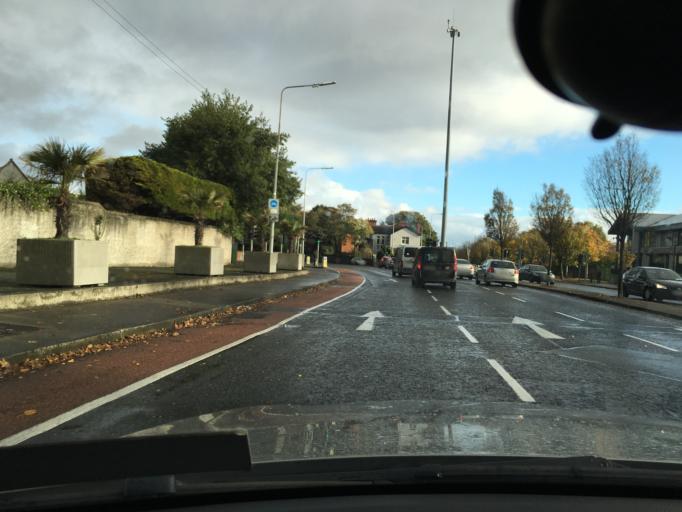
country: IE
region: Leinster
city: Cabra
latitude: 53.3620
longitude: -6.2993
